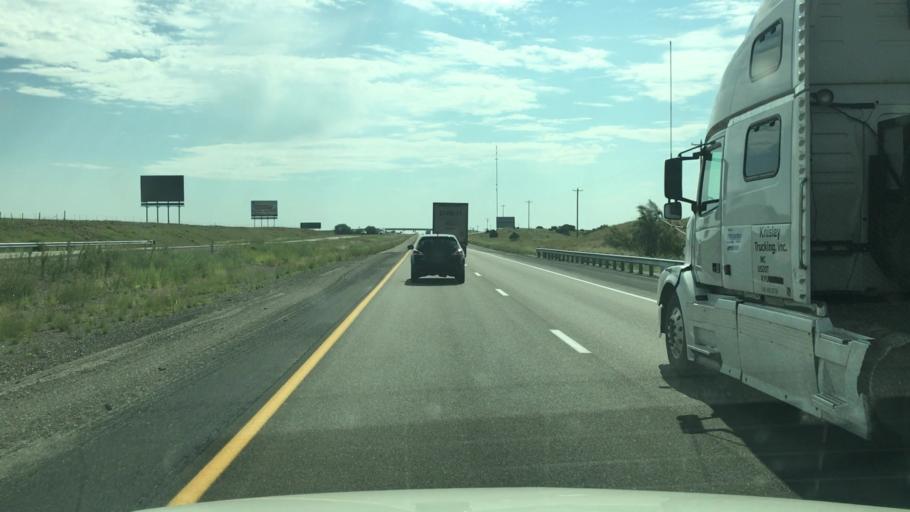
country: US
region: New Mexico
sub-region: San Miguel County
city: Las Vegas
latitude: 34.9920
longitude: -105.3057
